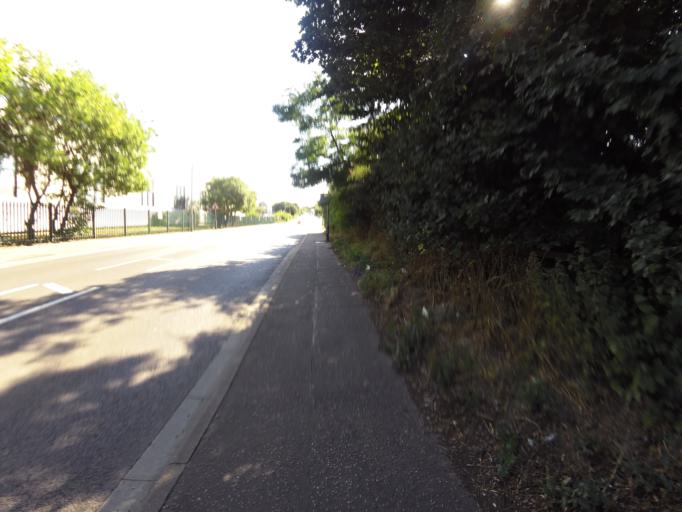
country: GB
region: England
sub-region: Essex
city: Witham
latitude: 51.8068
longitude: 0.6496
